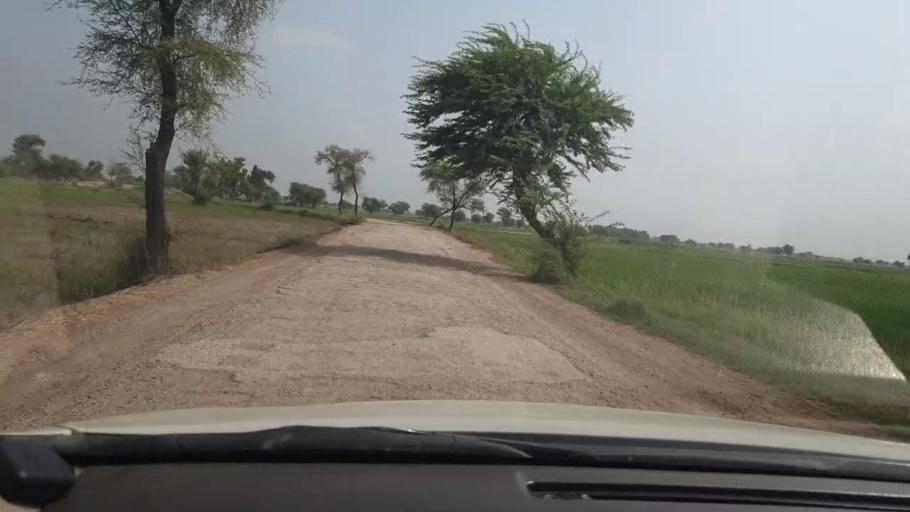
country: PK
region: Sindh
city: Shikarpur
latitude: 27.9974
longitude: 68.5953
